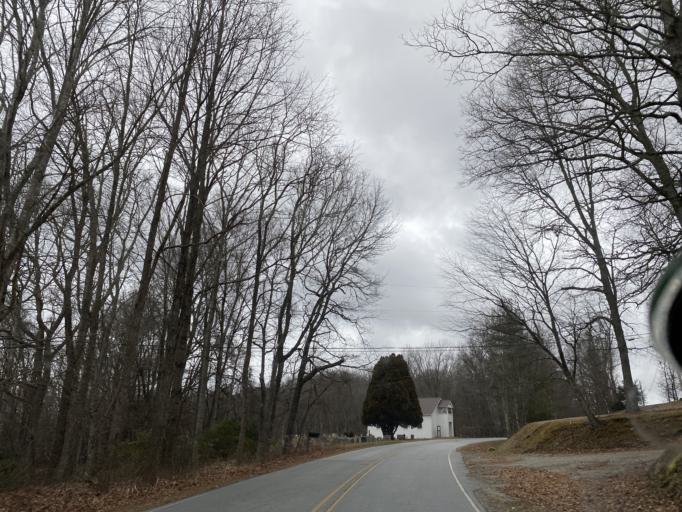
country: US
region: North Carolina
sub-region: Jackson County
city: Cullowhee
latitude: 35.2132
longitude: -83.1831
